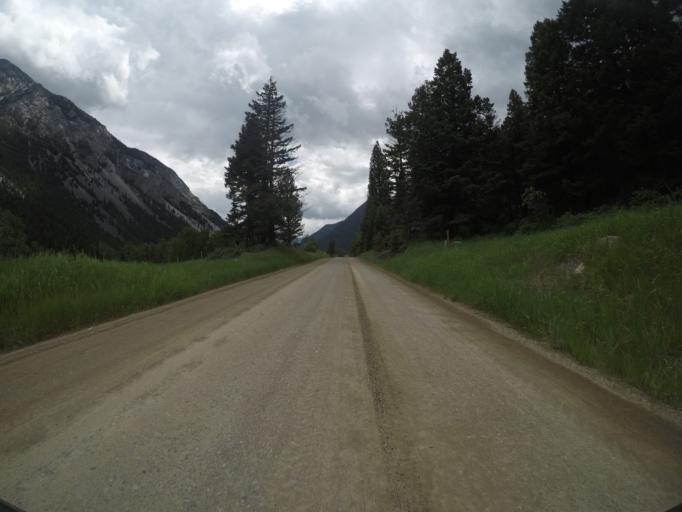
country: US
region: Montana
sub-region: Park County
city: Livingston
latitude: 45.5087
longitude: -110.2271
